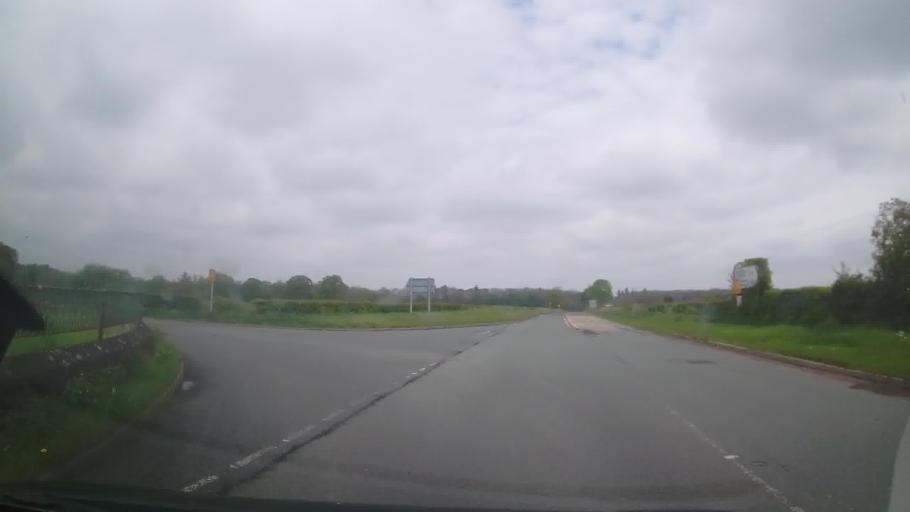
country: GB
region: Wales
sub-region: Wrexham
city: Overton
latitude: 52.9816
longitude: -2.9635
